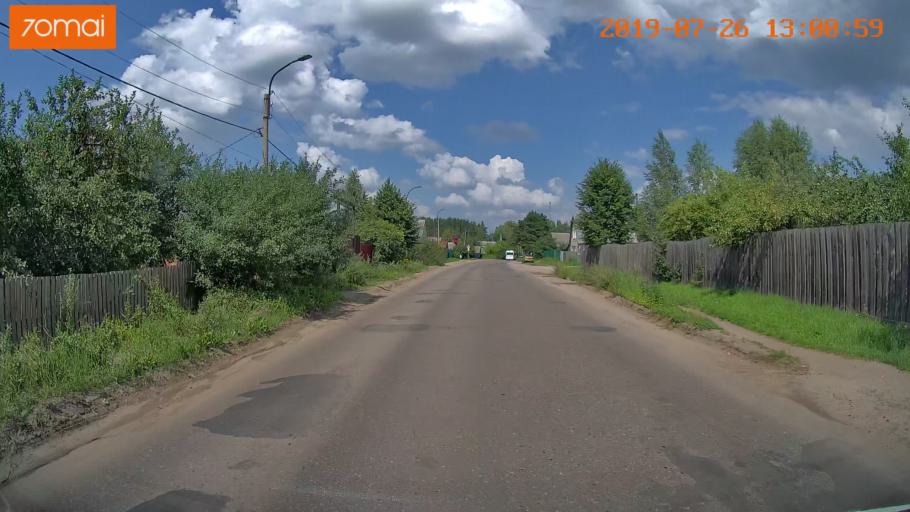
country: RU
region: Ivanovo
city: Bogorodskoye
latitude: 57.0363
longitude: 41.0127
